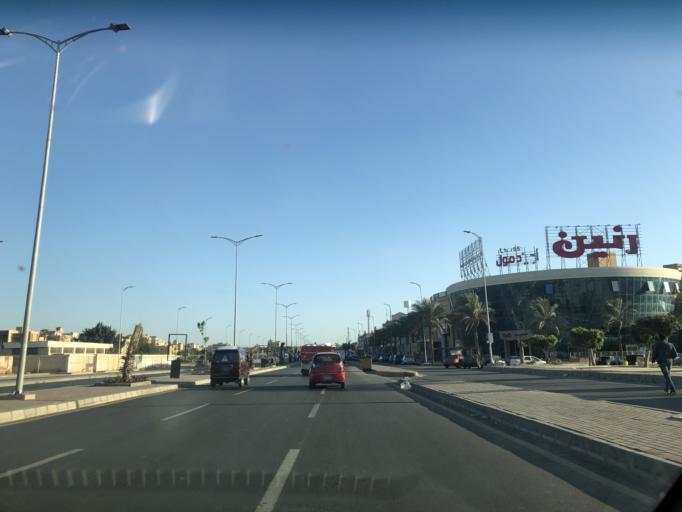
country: EG
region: Al Jizah
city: Madinat Sittah Uktubar
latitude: 29.9494
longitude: 30.9132
